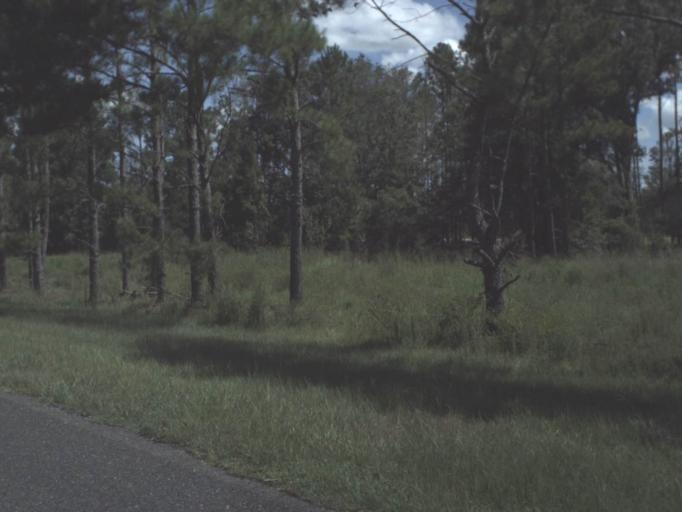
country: US
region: Florida
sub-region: Levy County
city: Chiefland
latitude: 29.4248
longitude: -82.8280
